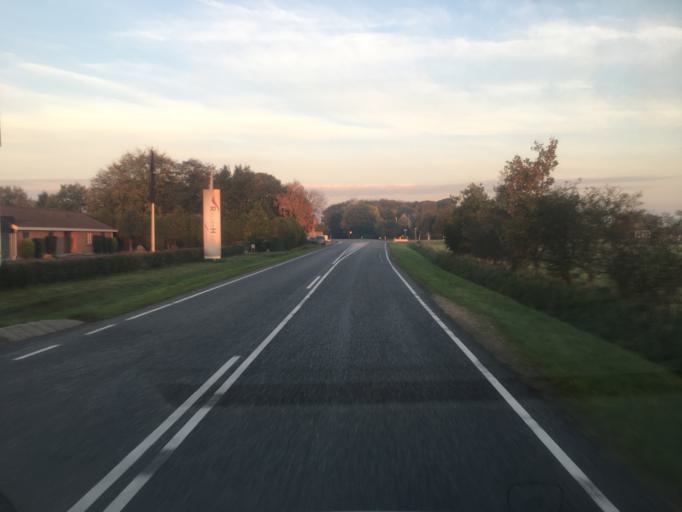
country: DK
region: South Denmark
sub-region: Tonder Kommune
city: Logumkloster
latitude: 55.0389
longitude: 9.0282
